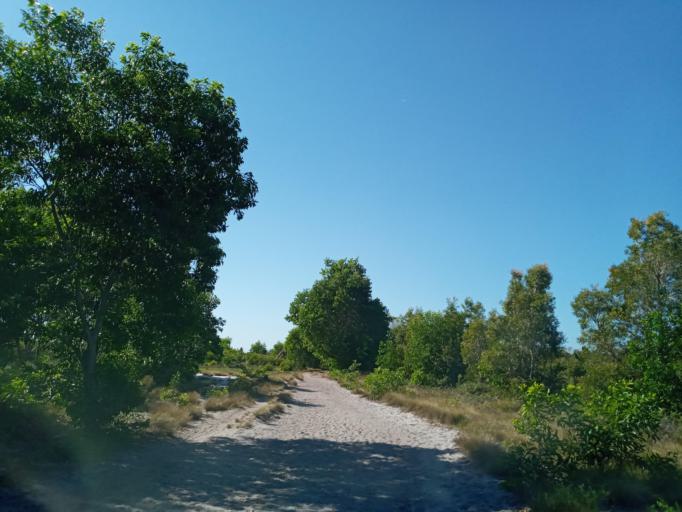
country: MG
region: Anosy
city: Fort Dauphin
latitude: -24.9063
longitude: 47.0976
